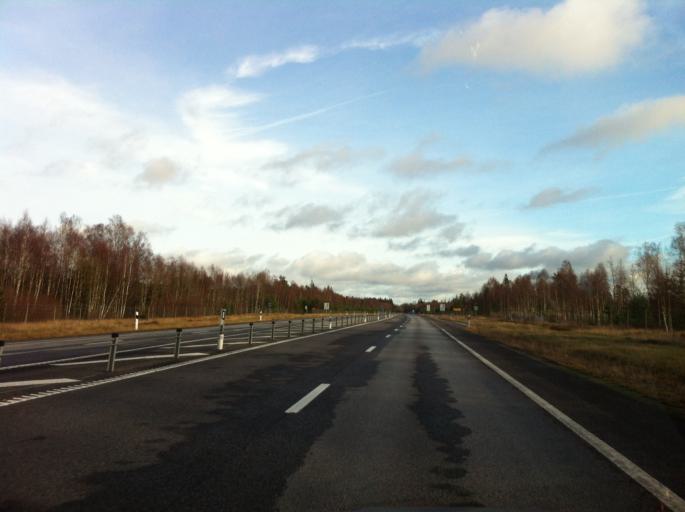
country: SE
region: Kronoberg
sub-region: Alvesta Kommun
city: Vislanda
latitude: 56.6747
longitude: 14.3141
